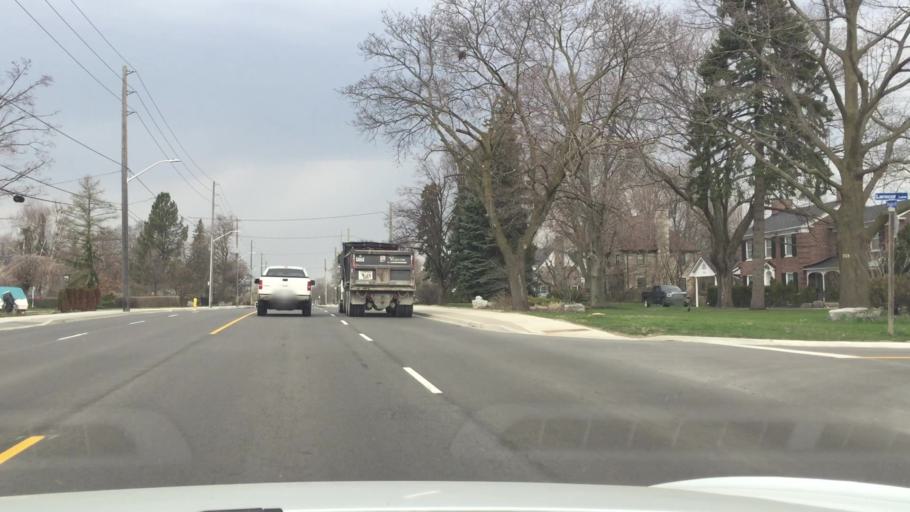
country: CA
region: Ontario
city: Oshawa
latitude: 43.9166
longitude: -78.8717
